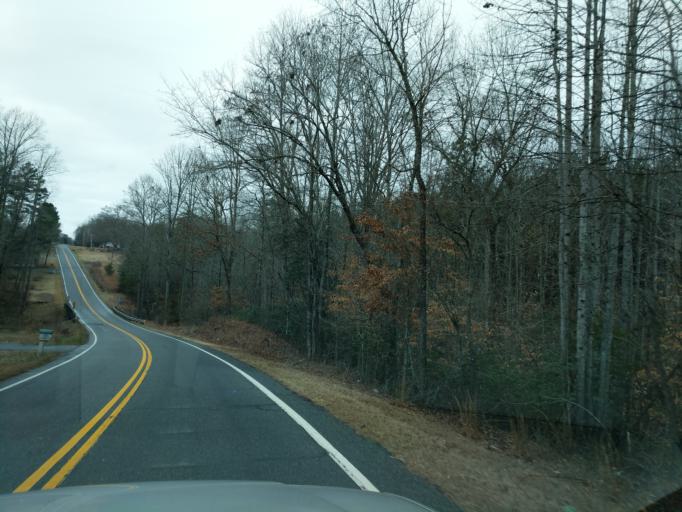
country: US
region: South Carolina
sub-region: Oconee County
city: Walhalla
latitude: 34.8091
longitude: -83.0563
